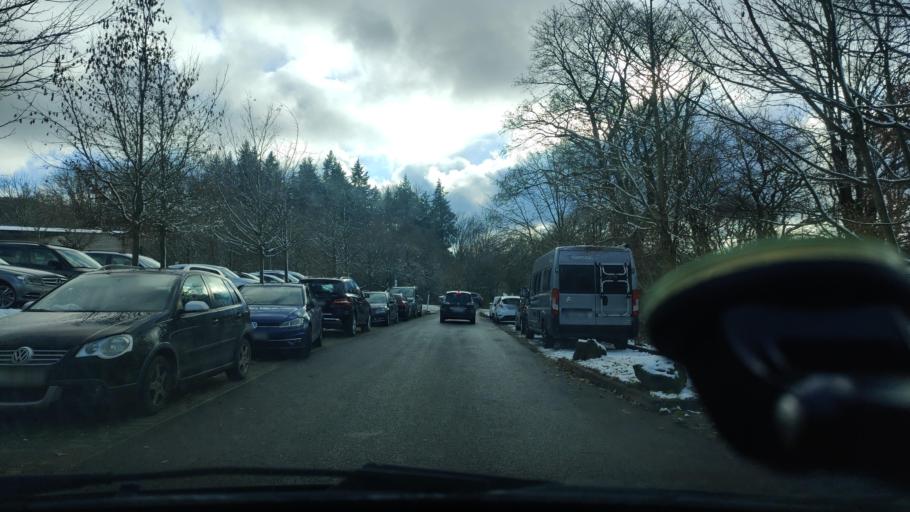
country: DE
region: Hesse
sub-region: Regierungsbezirk Kassel
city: Baunatal
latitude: 51.3177
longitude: 9.3899
